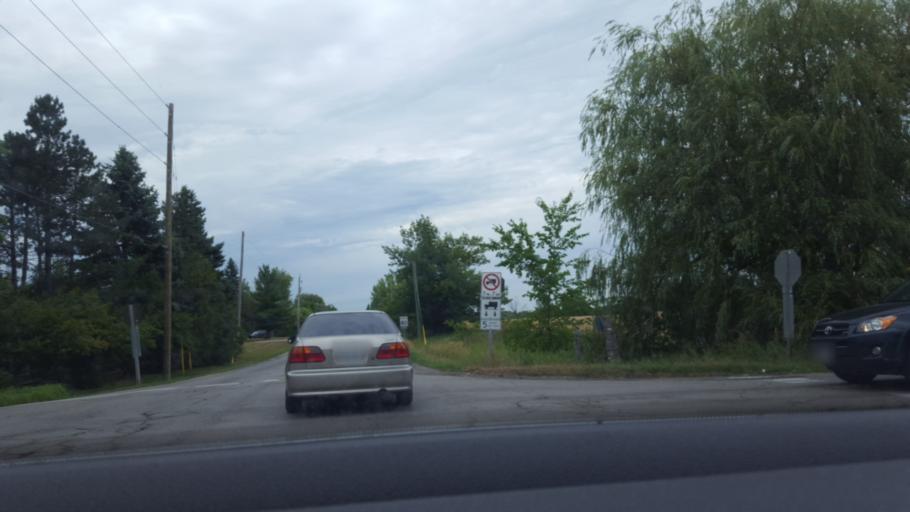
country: CA
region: Ontario
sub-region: Halton
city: Milton
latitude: 43.5980
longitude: -79.8574
